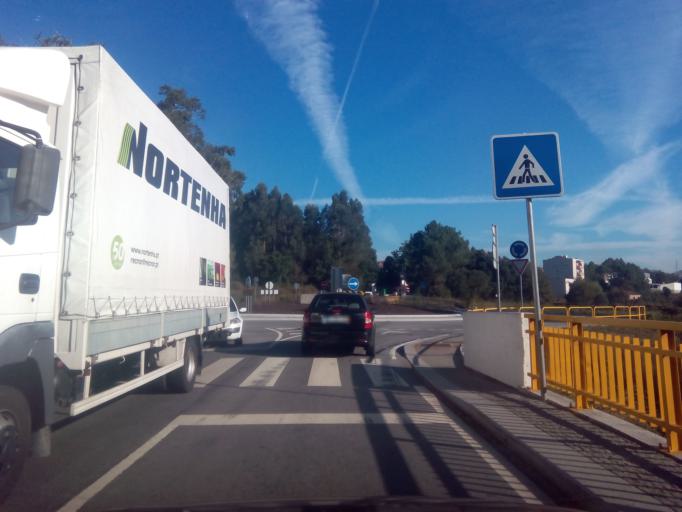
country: PT
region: Porto
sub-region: Paredes
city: Gandra
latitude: 41.1856
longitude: -8.4374
